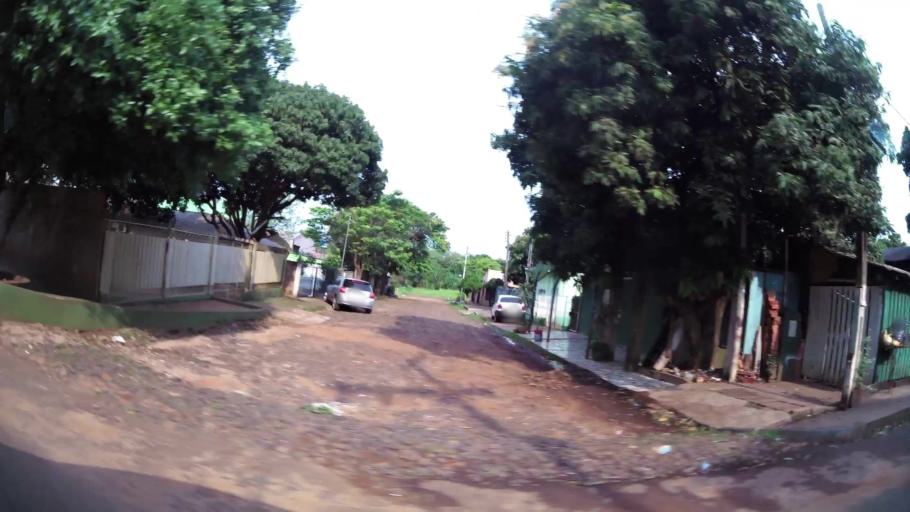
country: PY
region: Alto Parana
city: Ciudad del Este
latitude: -25.4973
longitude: -54.6596
